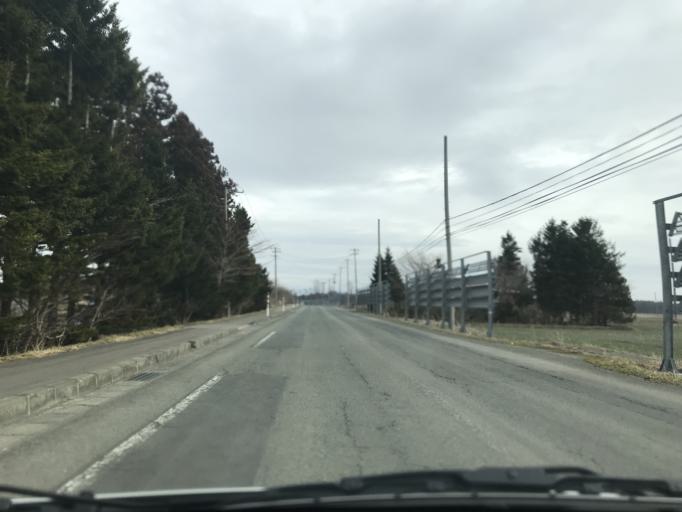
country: JP
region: Iwate
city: Kitakami
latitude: 39.3274
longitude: 140.9991
